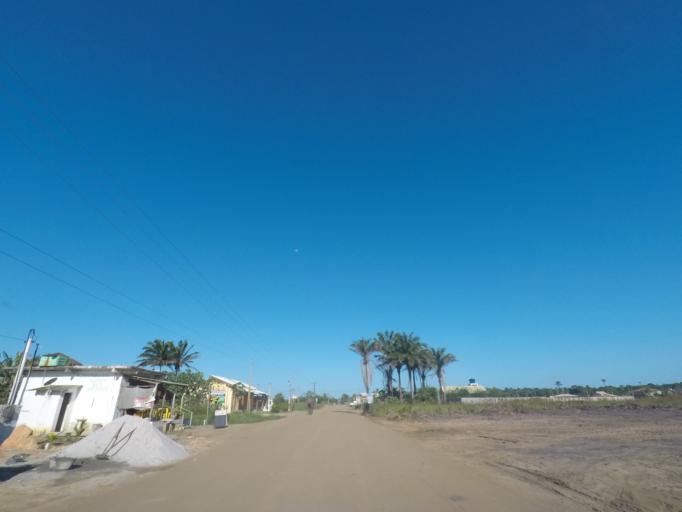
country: BR
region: Bahia
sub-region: Camamu
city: Camamu
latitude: -13.9319
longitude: -38.9397
